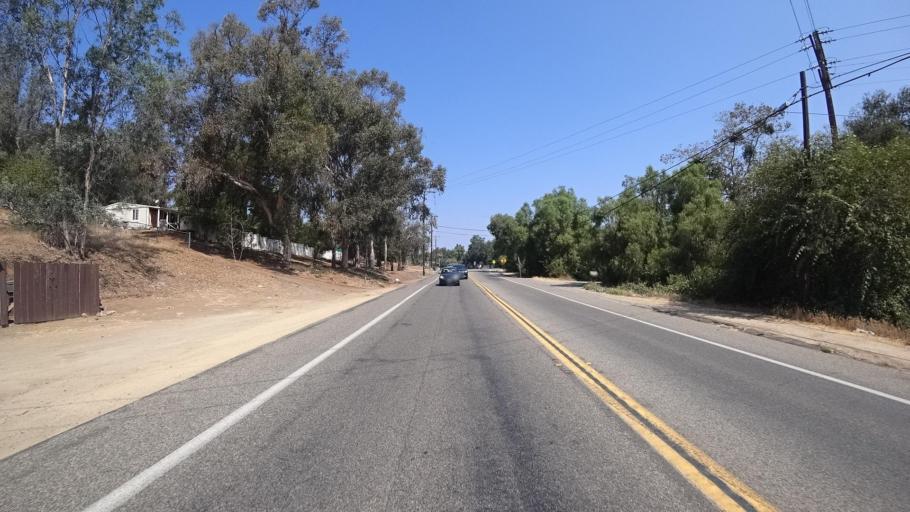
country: US
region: California
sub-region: San Diego County
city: Fallbrook
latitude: 33.3442
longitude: -117.2414
